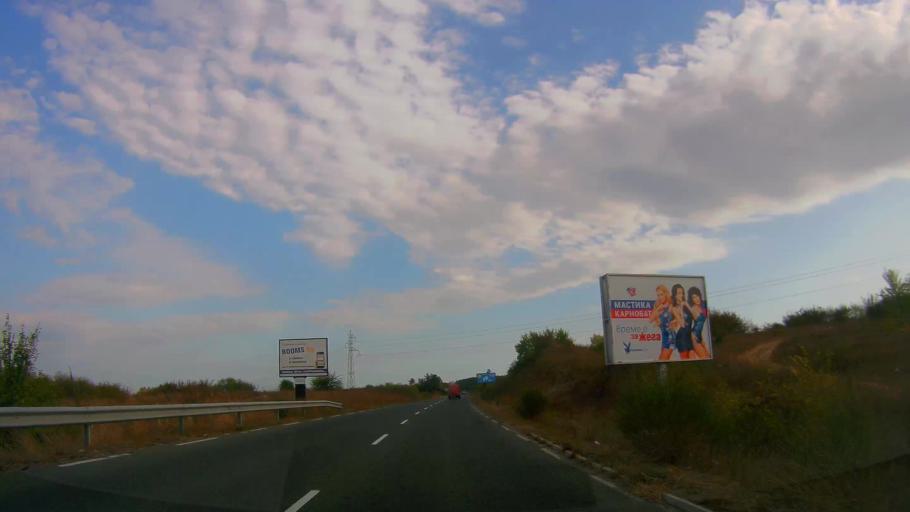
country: BG
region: Burgas
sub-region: Obshtina Sozopol
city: Sozopol
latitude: 42.3972
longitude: 27.6752
